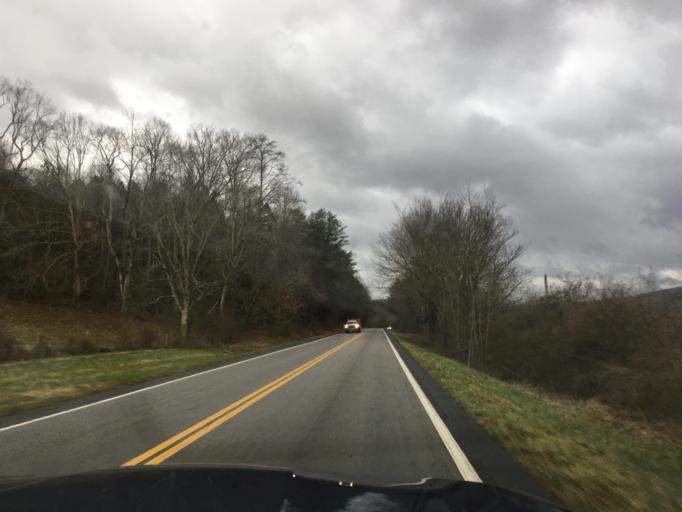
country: US
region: Tennessee
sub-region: Cumberland County
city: Lake Tansi
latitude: 35.8531
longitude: -84.9189
